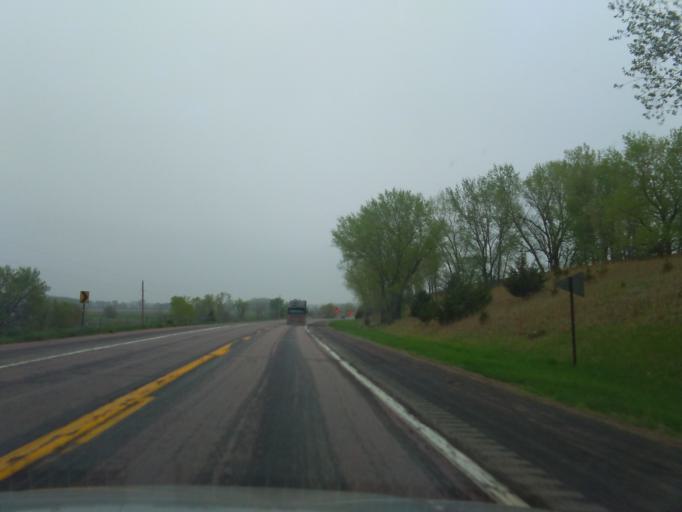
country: US
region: Nebraska
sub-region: Burt County
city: Oakland
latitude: 41.8003
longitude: -96.4821
